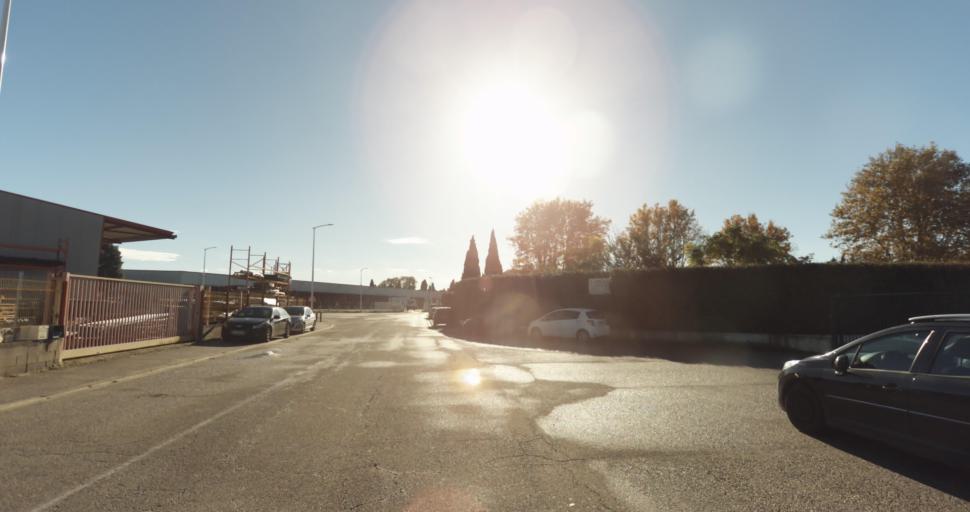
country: FR
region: Provence-Alpes-Cote d'Azur
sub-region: Departement des Bouches-du-Rhone
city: Rognonas
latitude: 43.8981
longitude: 4.8147
